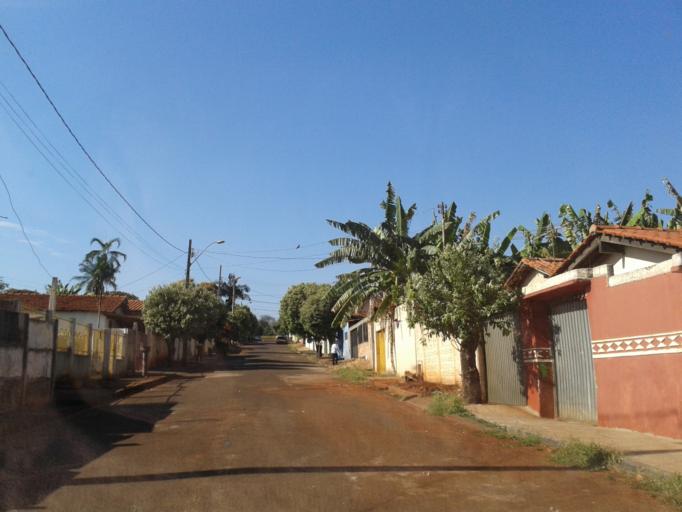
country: BR
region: Minas Gerais
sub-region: Ituiutaba
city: Ituiutaba
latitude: -18.9668
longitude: -49.4780
